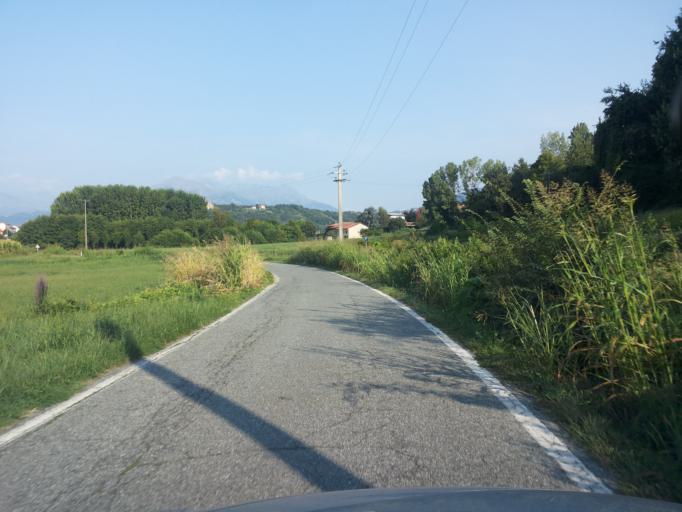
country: IT
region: Piedmont
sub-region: Provincia di Torino
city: Bollengo
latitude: 45.4692
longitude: 7.9565
